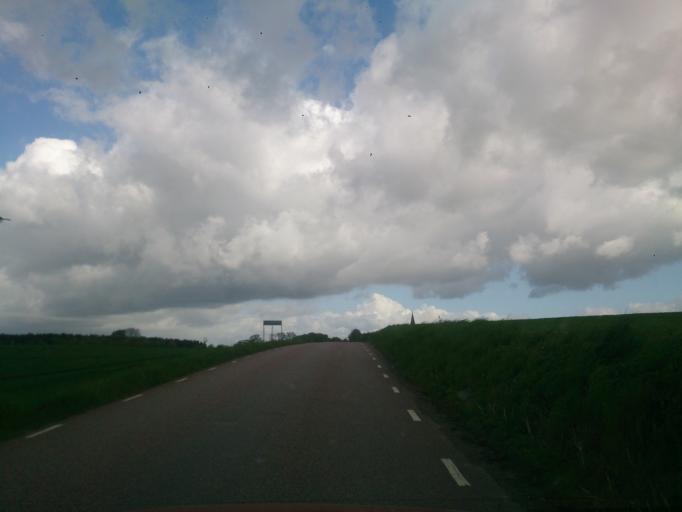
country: SE
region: Skane
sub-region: Ystads Kommun
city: Ystad
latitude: 55.4497
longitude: 13.7145
